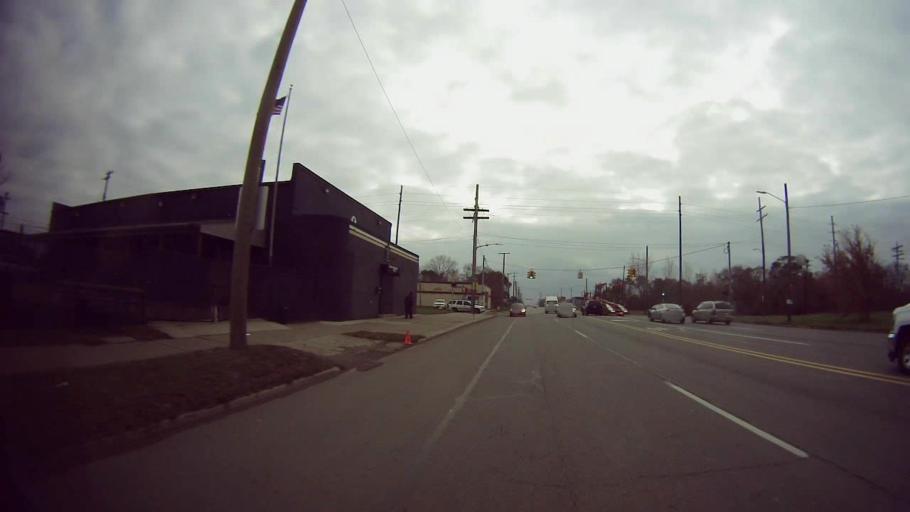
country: US
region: Michigan
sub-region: Wayne County
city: Hamtramck
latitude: 42.4056
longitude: -83.0231
